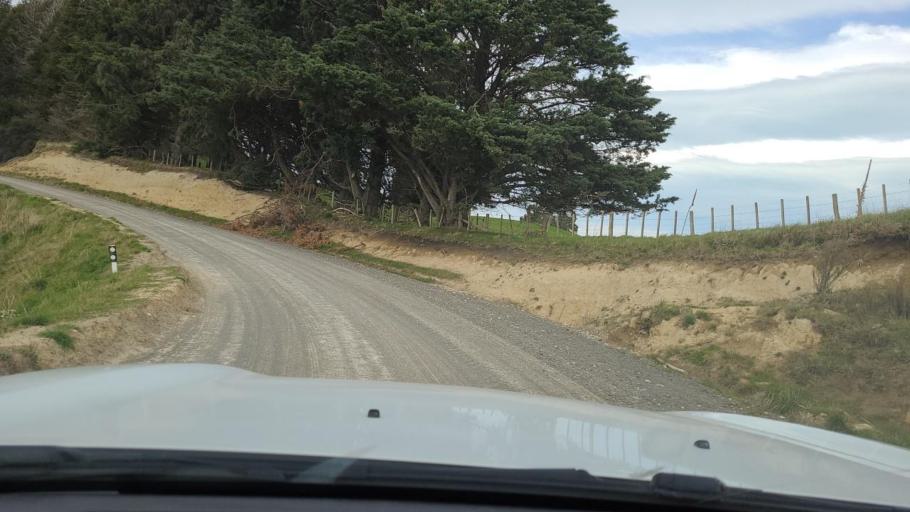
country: NZ
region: Hawke's Bay
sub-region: Napier City
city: Napier
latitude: -39.3220
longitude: 176.8355
